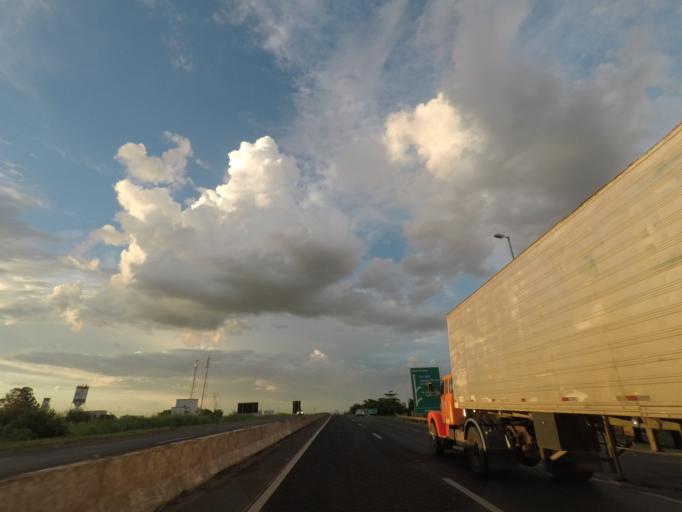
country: BR
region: Minas Gerais
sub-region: Uberaba
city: Uberaba
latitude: -19.7744
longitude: -47.9724
